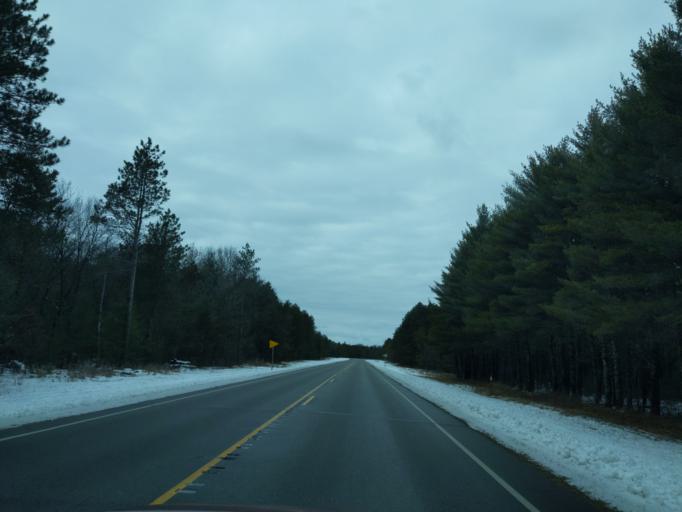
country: US
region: Wisconsin
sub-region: Waushara County
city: Wautoma
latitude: 43.9614
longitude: -89.3215
